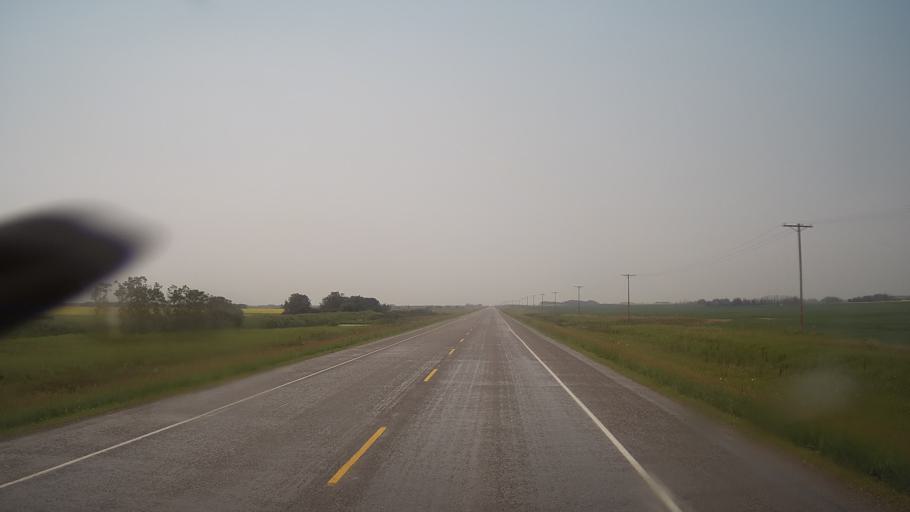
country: CA
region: Saskatchewan
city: Biggar
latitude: 52.1528
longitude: -108.2417
